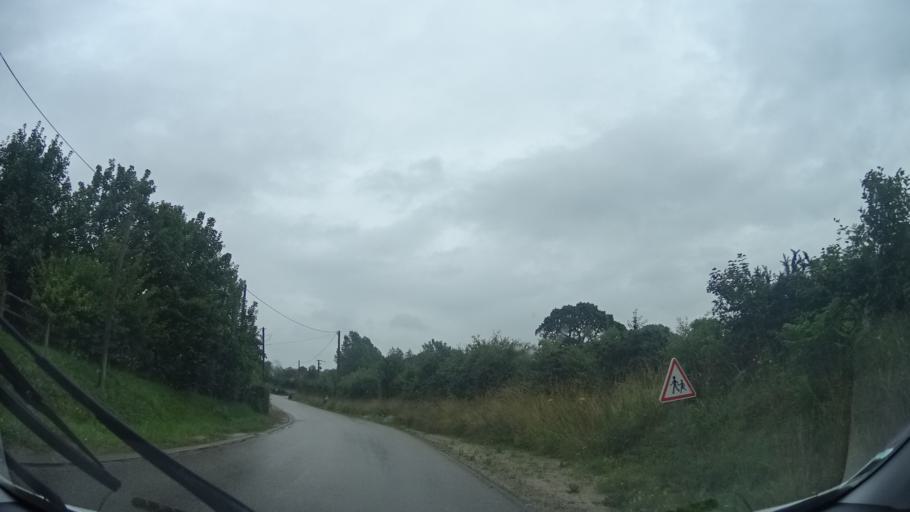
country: FR
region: Lower Normandy
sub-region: Departement de la Manche
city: Urville-Nacqueville
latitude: 49.5961
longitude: -1.7562
